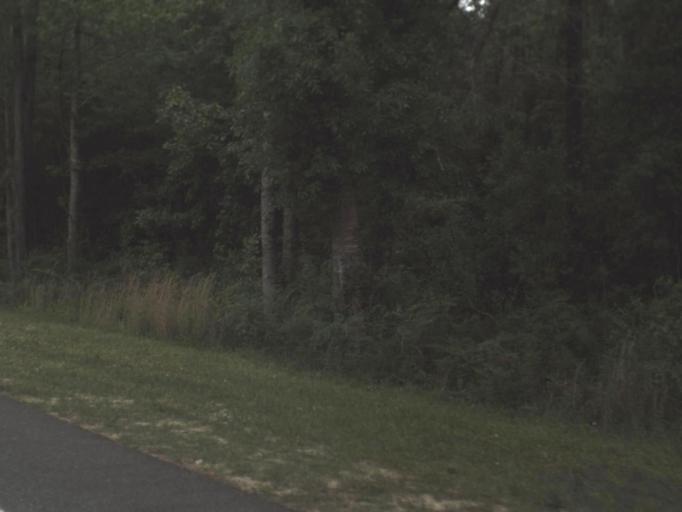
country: US
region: Florida
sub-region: Santa Rosa County
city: Point Baker
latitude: 30.7871
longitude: -87.0415
